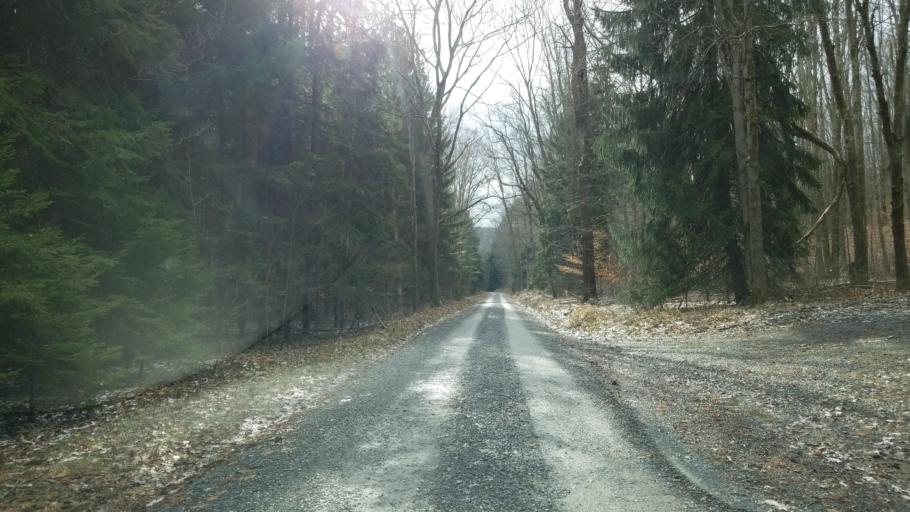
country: US
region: Pennsylvania
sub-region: Clearfield County
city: Clearfield
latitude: 41.1895
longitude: -78.5142
